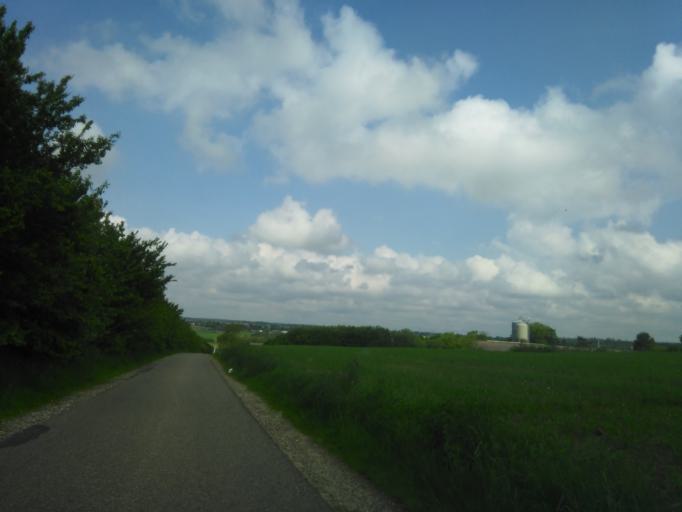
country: DK
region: Central Jutland
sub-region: Arhus Kommune
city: Sabro
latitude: 56.2073
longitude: 9.9891
